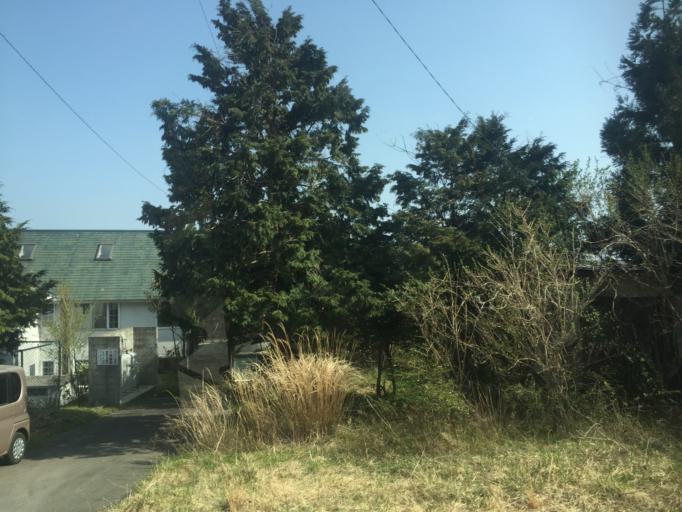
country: JP
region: Shizuoka
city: Ito
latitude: 34.9047
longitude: 139.1034
